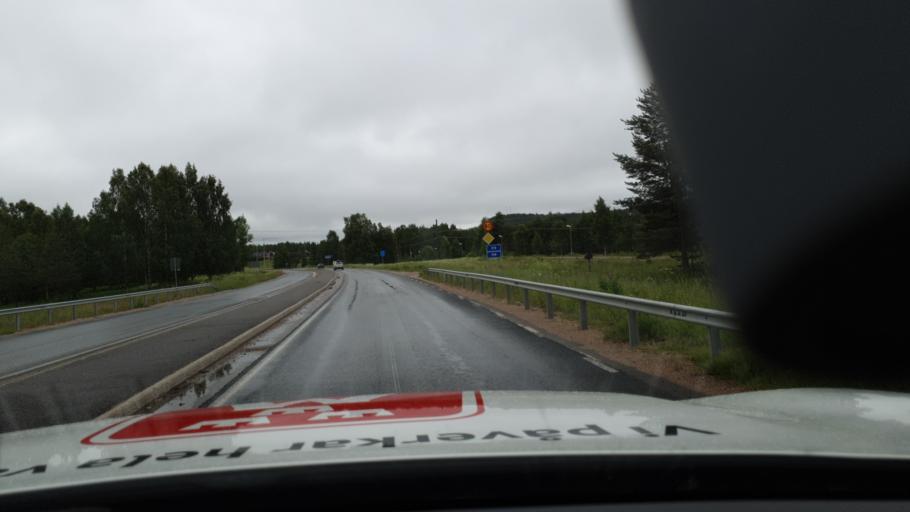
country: SE
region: Norrbotten
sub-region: Overtornea Kommun
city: OEvertornea
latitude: 66.3963
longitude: 23.6262
